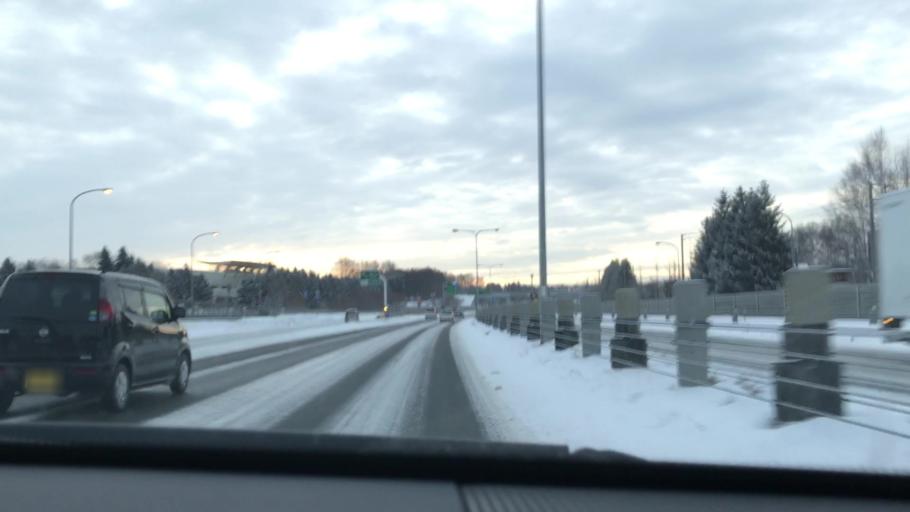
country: JP
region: Hokkaido
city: Kitahiroshima
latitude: 43.0204
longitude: 141.4599
